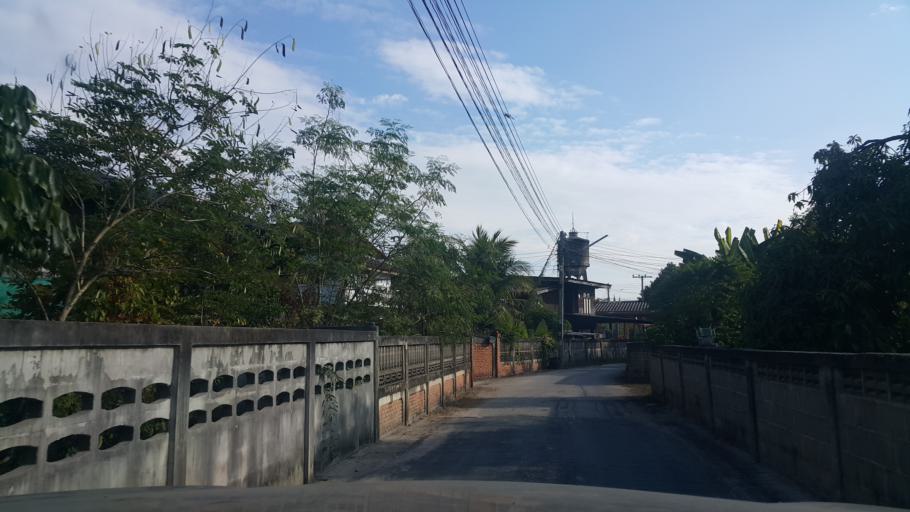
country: TH
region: Lampang
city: Hang Chat
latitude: 18.3121
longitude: 99.3531
